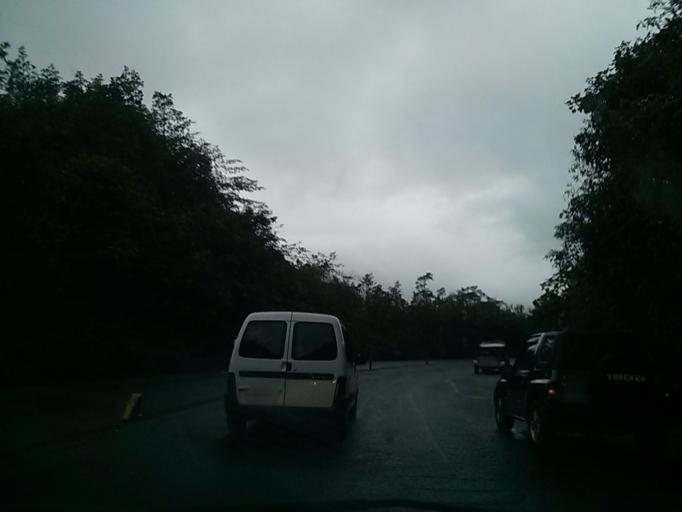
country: CR
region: San Jose
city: Dulce Nombre de Jesus
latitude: 10.0680
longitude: -83.9907
